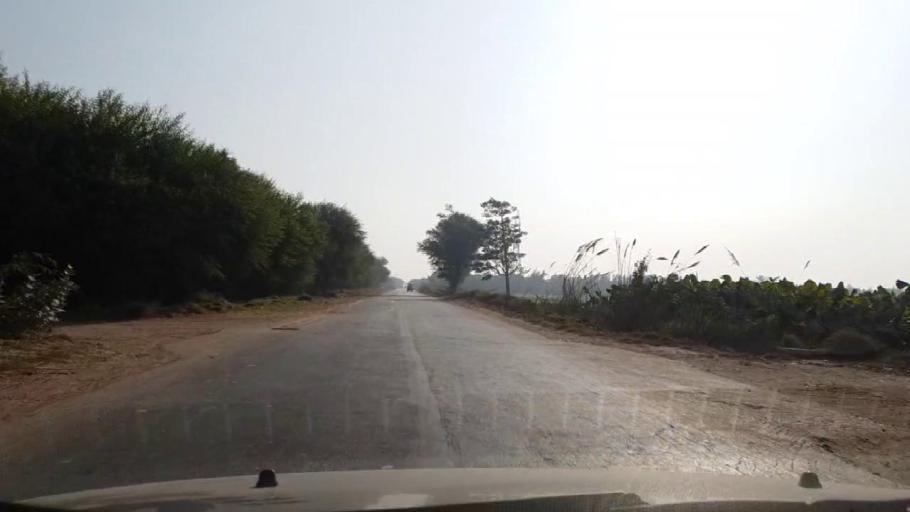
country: PK
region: Sindh
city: Matiari
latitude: 25.5960
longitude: 68.4639
